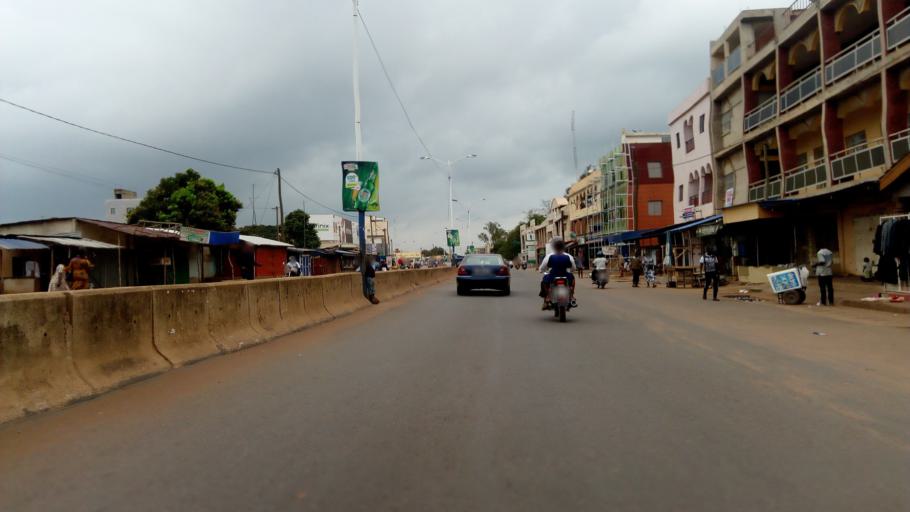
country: TG
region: Maritime
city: Lome
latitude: 6.2246
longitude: 1.2103
